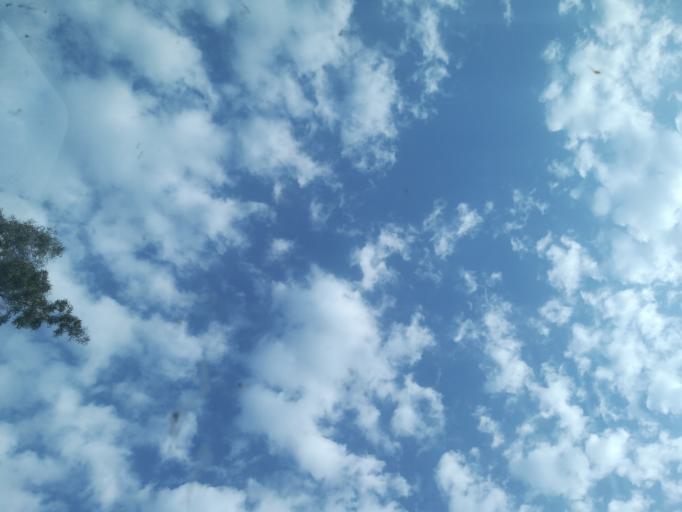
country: TR
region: Osmaniye
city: Osmaniye
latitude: 37.0457
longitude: 36.2264
